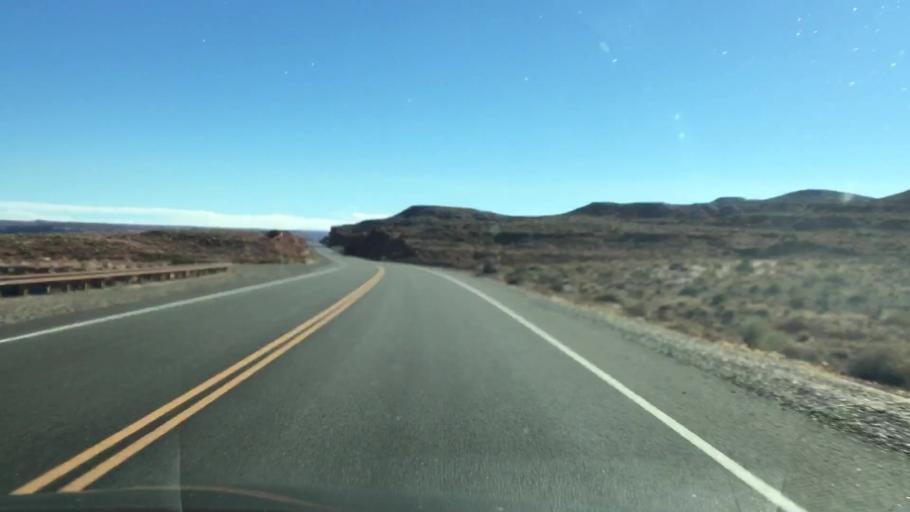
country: US
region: Arizona
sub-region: Coconino County
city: Page
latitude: 36.9832
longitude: -111.4948
